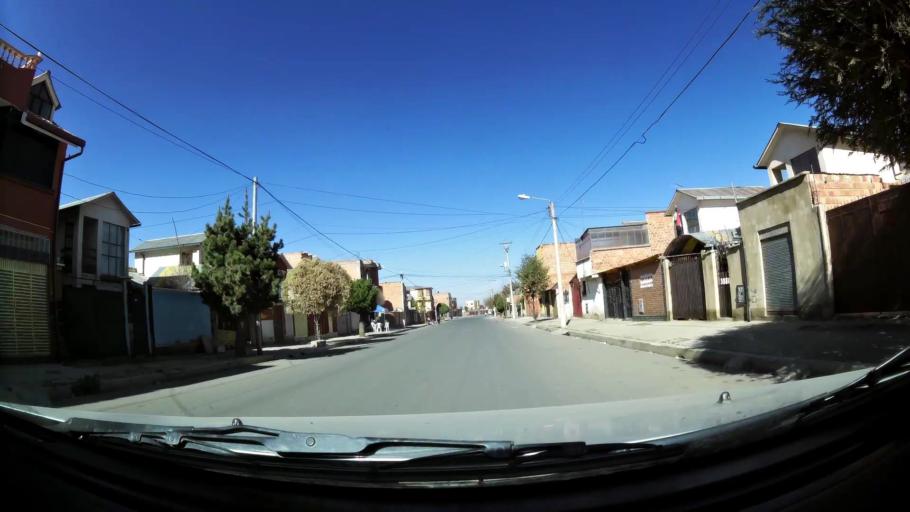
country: BO
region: La Paz
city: La Paz
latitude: -16.5259
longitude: -68.2089
